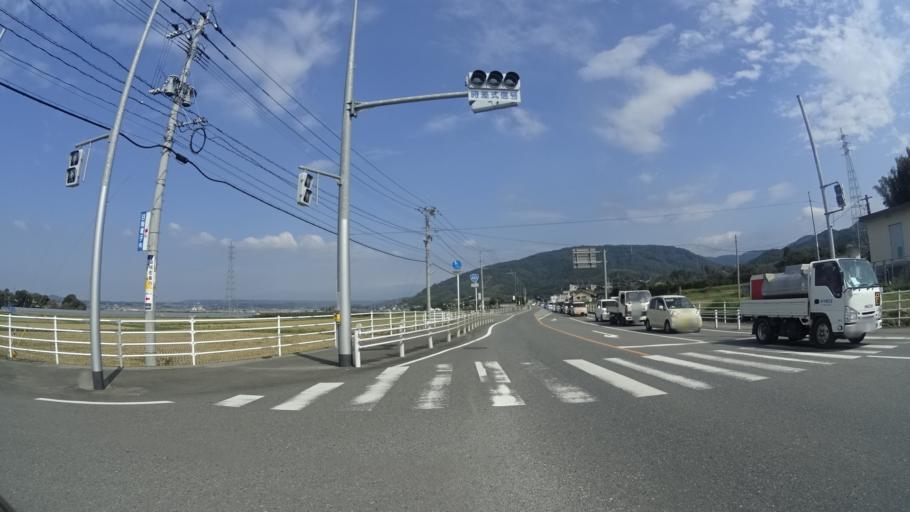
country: JP
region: Kumamoto
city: Kumamoto
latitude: 32.7555
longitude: 130.8053
